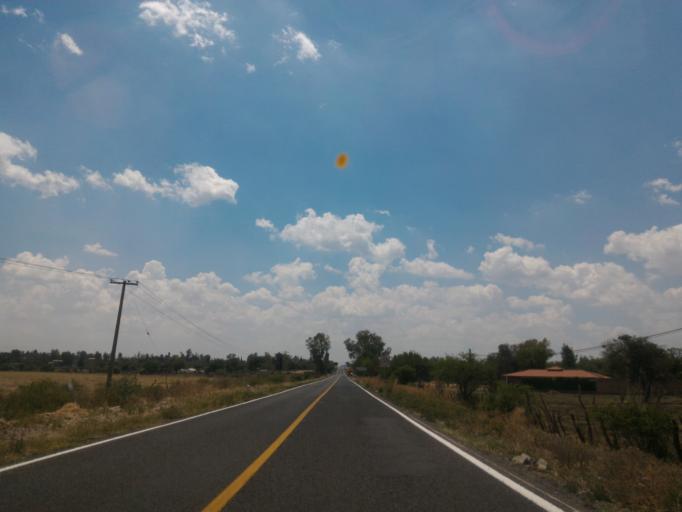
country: MX
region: Guanajuato
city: Ciudad Manuel Doblado
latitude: 20.7983
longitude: -101.9863
